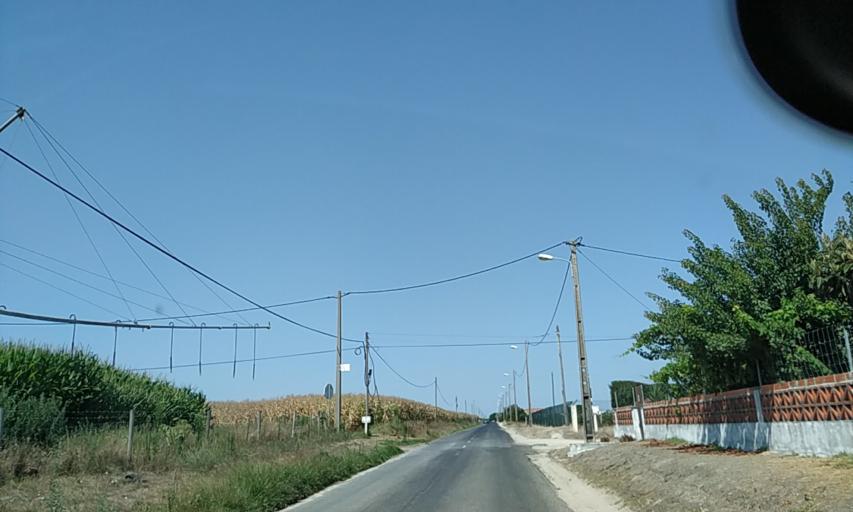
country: PT
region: Santarem
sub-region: Benavente
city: Poceirao
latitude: 38.7055
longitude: -8.7201
